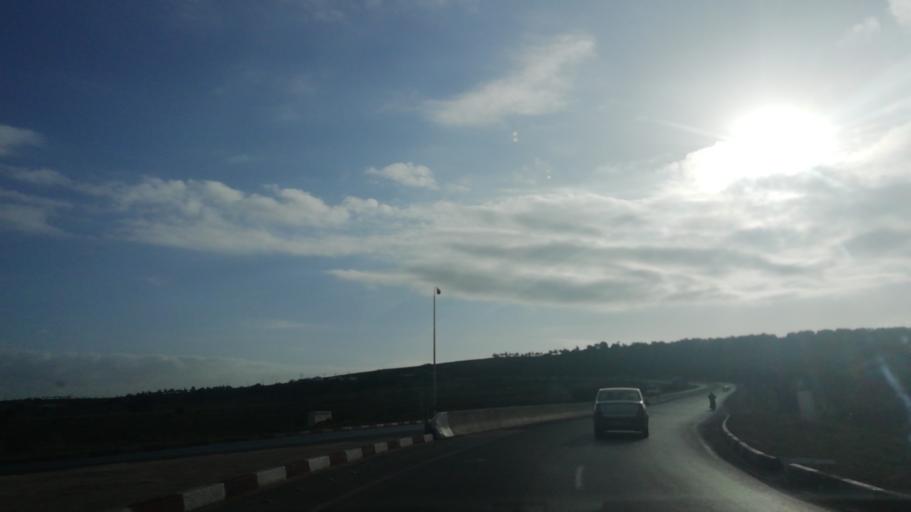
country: DZ
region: Mostaganem
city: Mostaganem
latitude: 36.0974
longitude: 0.2769
